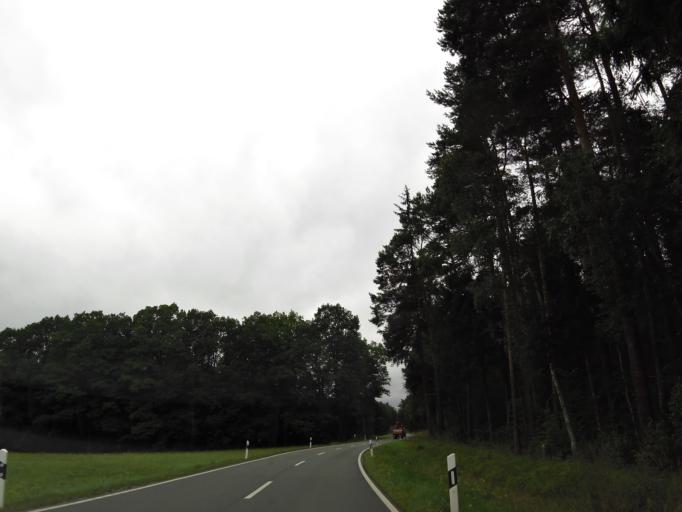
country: DE
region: Thuringia
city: Bad Klosterlausnitz
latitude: 50.9298
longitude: 11.8623
